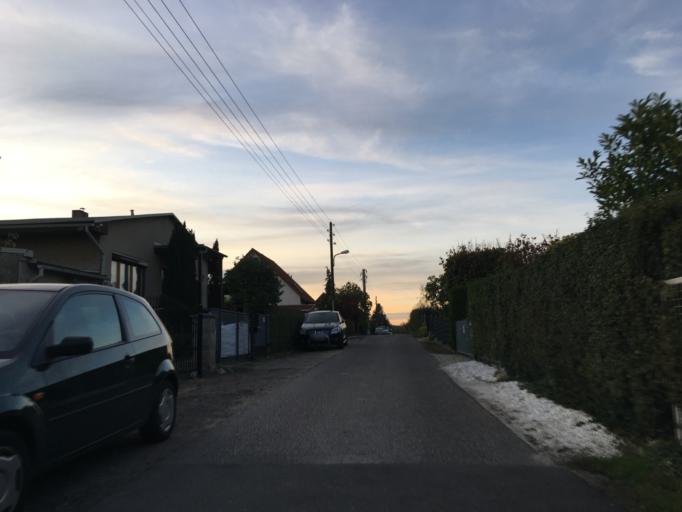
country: DE
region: Berlin
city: Buchholz
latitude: 52.6170
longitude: 13.4265
